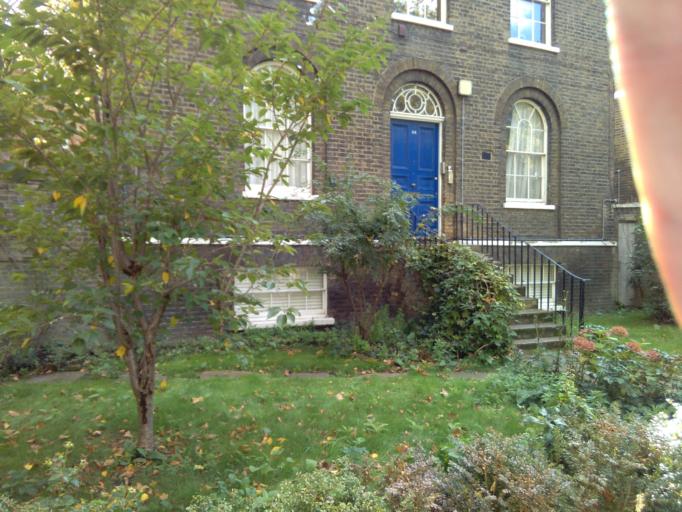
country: GB
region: England
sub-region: Greater London
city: Kennington
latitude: 51.4777
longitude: -0.1069
